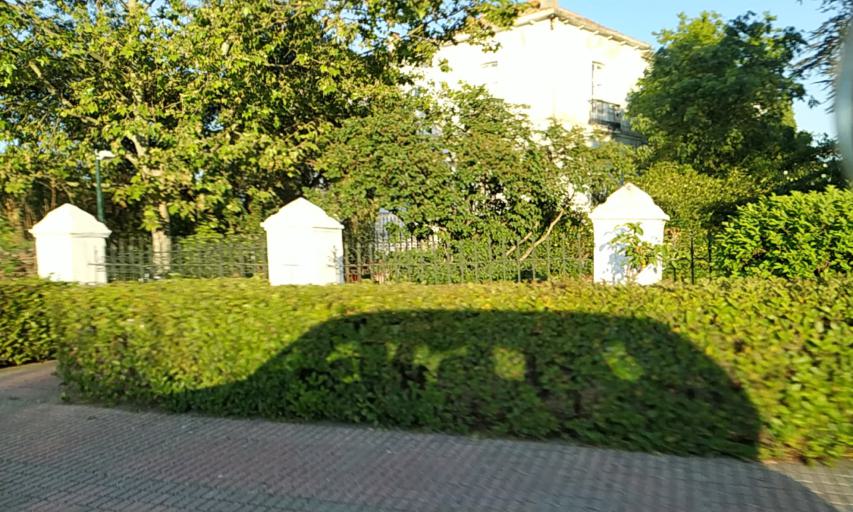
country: ES
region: Extremadura
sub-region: Provincia de Caceres
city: Valencia de Alcantara
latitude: 39.4091
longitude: -7.2470
